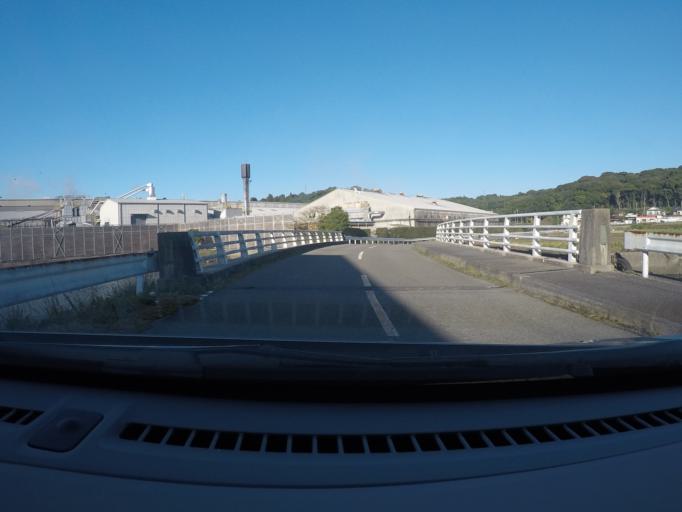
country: JP
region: Kumamoto
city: Minamata
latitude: 32.1781
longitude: 130.3801
